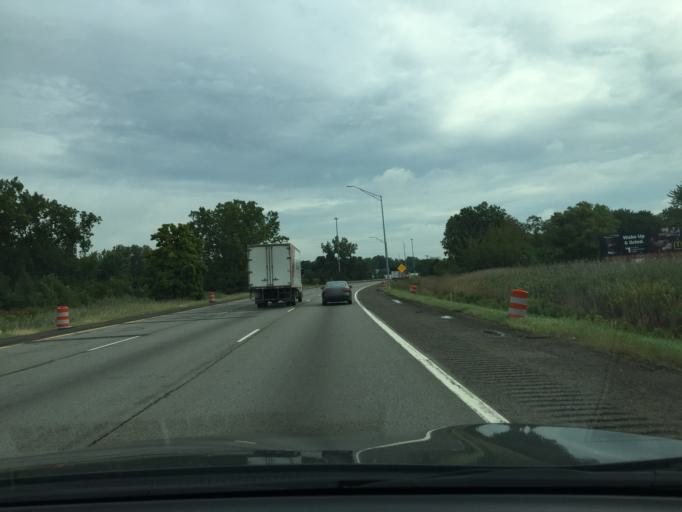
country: US
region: Michigan
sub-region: Wayne County
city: Taylor
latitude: 42.2591
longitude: -83.2925
